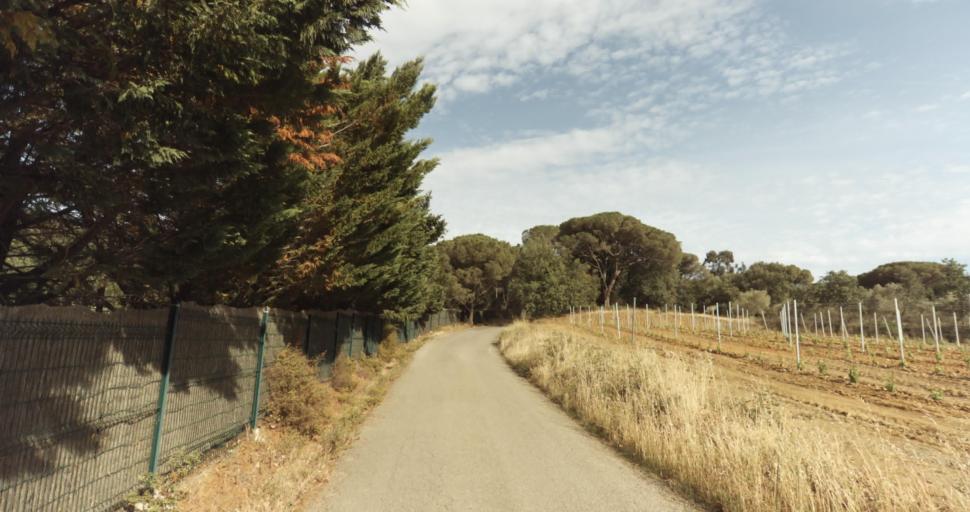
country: FR
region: Provence-Alpes-Cote d'Azur
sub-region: Departement du Var
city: Gassin
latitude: 43.2253
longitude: 6.5772
